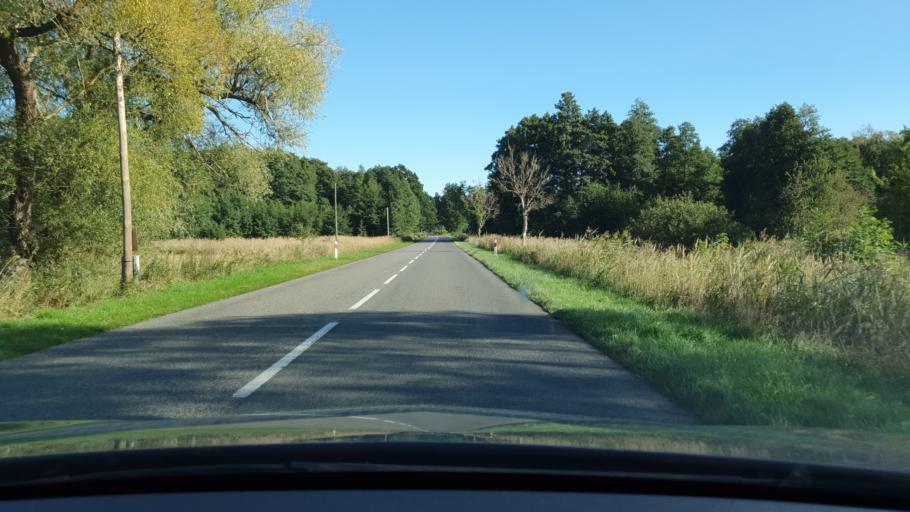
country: PL
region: West Pomeranian Voivodeship
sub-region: Powiat goleniowski
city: Przybiernow
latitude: 53.8301
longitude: 14.7757
